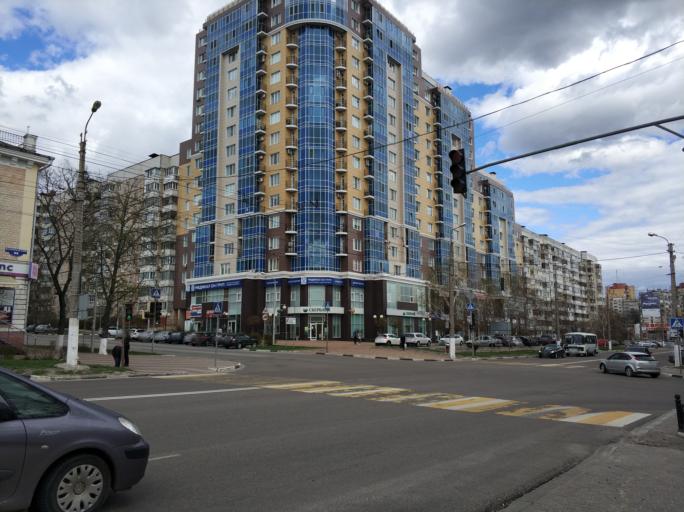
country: RU
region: Belgorod
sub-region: Belgorodskiy Rayon
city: Belgorod
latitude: 50.6017
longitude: 36.5943
